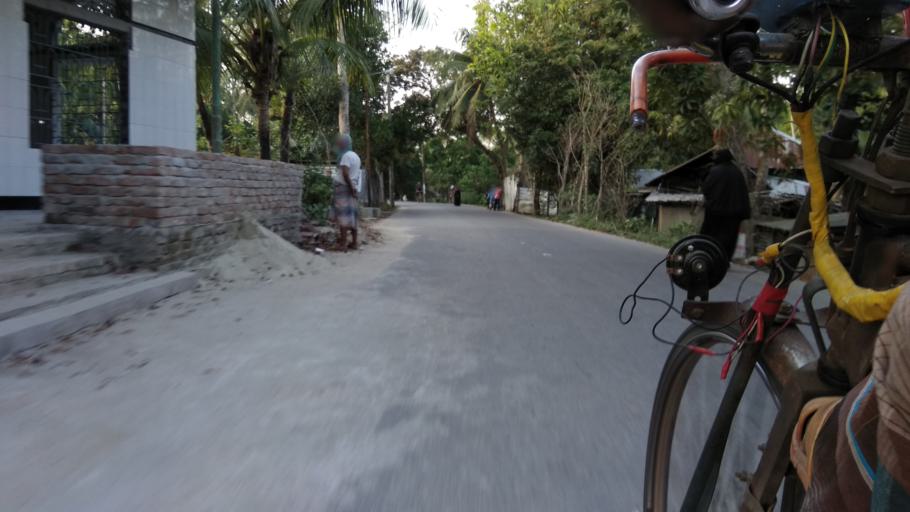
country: BD
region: Barisal
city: Mehendiganj
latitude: 22.9171
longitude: 90.4106
